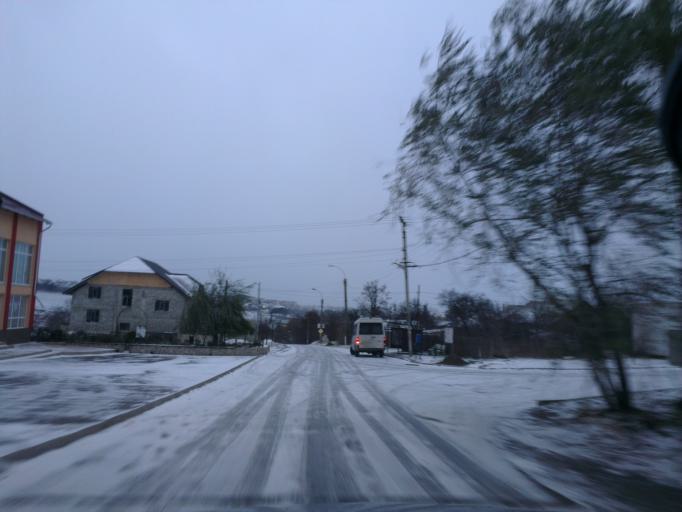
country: MD
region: Chisinau
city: Ciorescu
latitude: 47.1184
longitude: 28.8987
